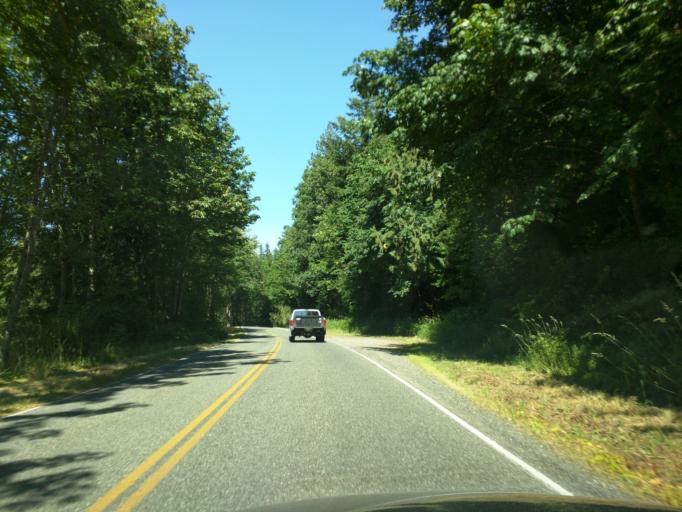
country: US
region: Washington
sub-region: Whatcom County
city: Peaceful Valley
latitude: 48.9541
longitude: -122.2085
